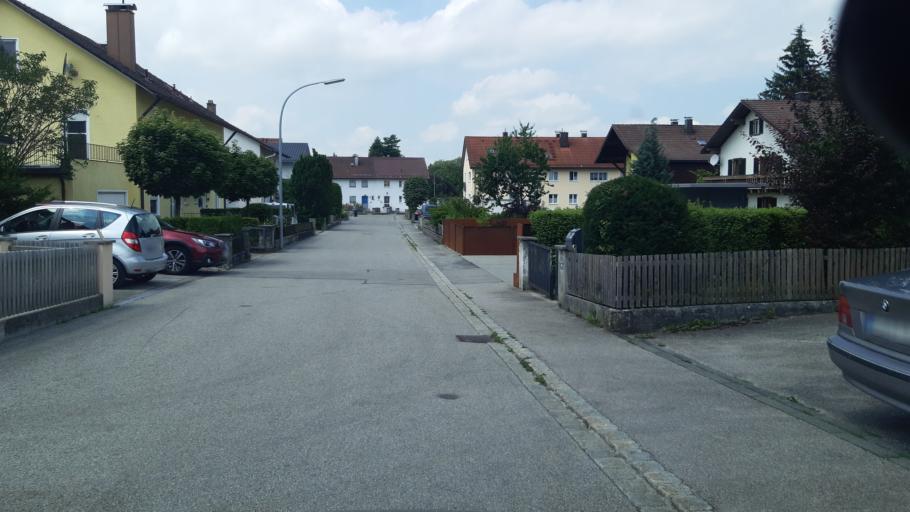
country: DE
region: Bavaria
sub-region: Swabia
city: Marktoberdorf
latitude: 47.7705
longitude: 10.6185
